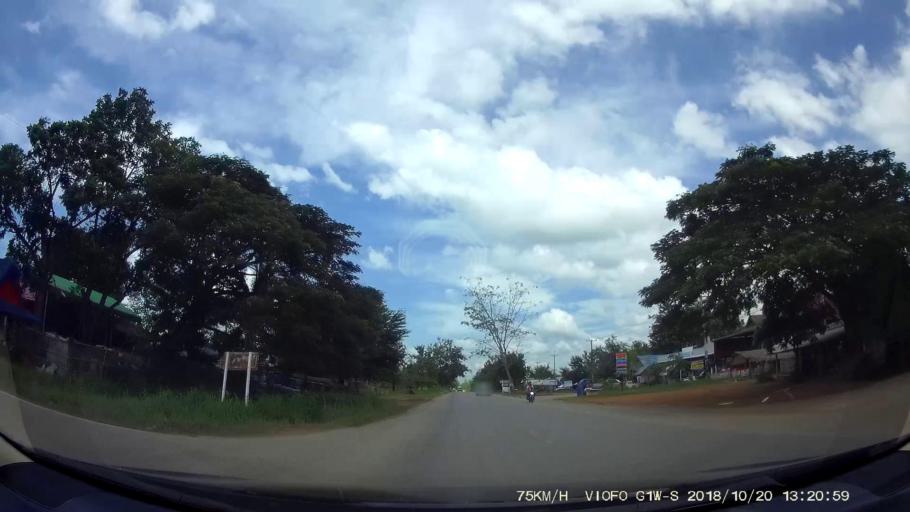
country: TH
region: Chaiyaphum
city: Khon San
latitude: 16.5538
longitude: 101.9069
